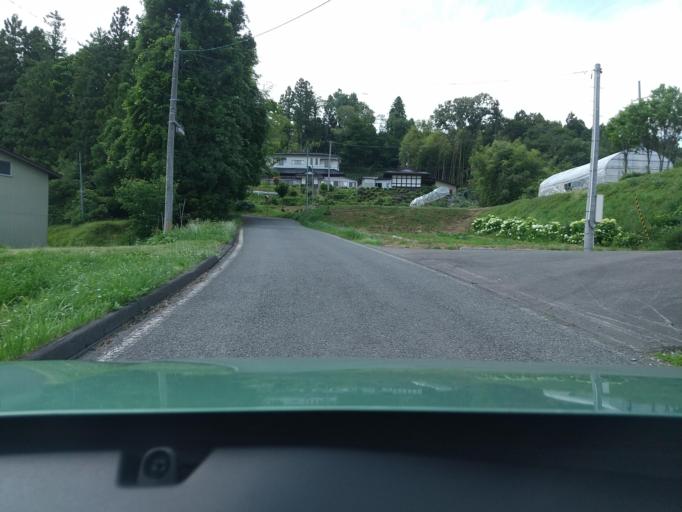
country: JP
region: Iwate
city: Ichinoseki
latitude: 39.0066
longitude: 141.2177
